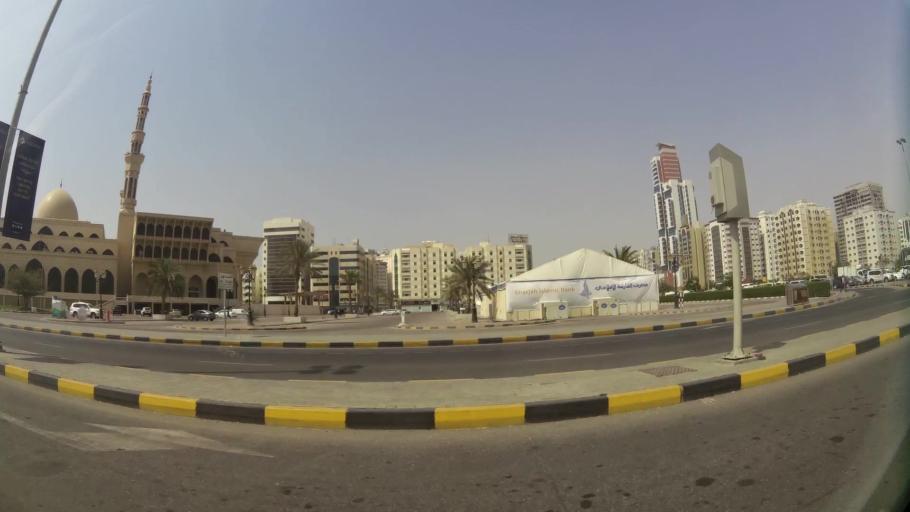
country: AE
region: Ash Shariqah
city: Sharjah
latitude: 25.3482
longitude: 55.3878
